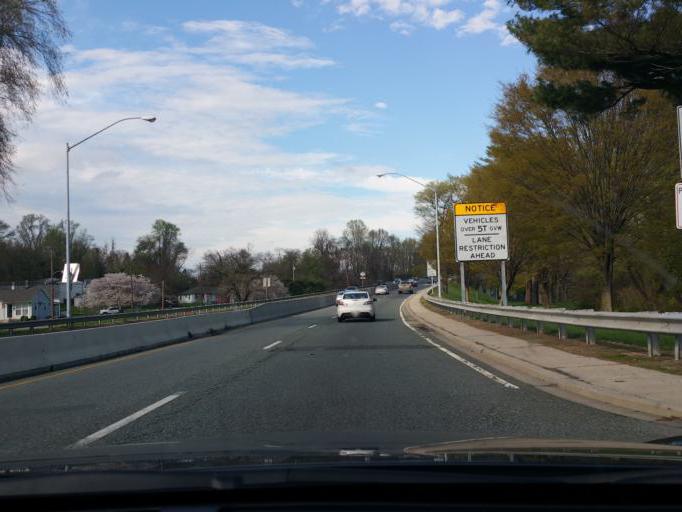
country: US
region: Maryland
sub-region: Harford County
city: Havre de Grace
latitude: 39.5551
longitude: -76.1001
